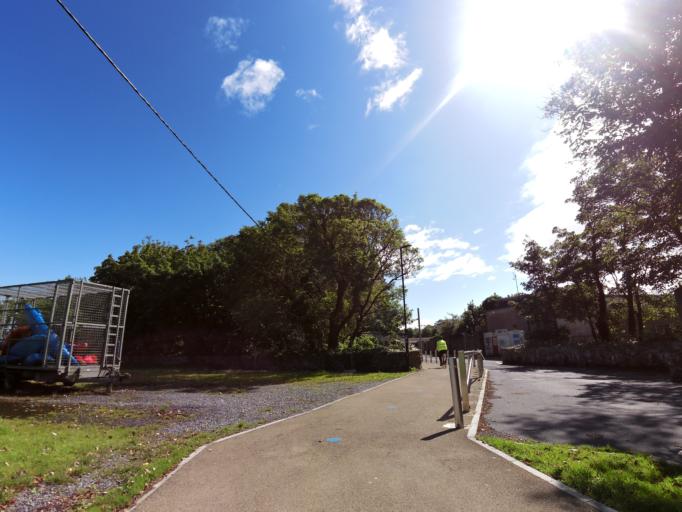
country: IE
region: Connaught
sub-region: County Galway
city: Gaillimh
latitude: 53.2767
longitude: -9.0577
